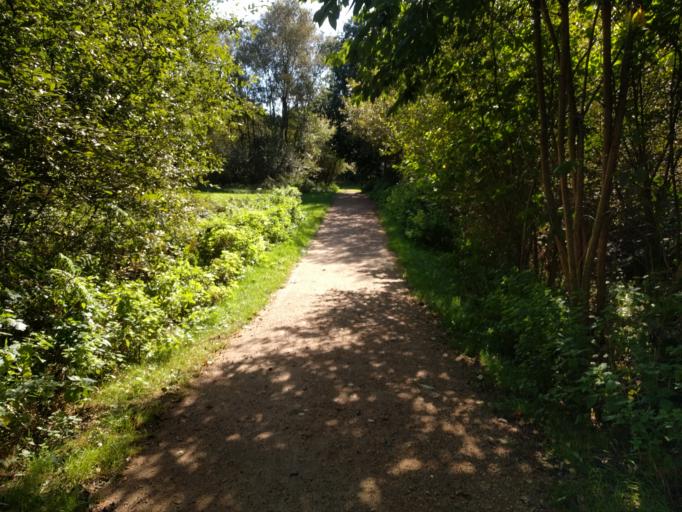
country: GB
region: England
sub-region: Warrington
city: Culcheth
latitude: 53.4211
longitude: -2.5086
